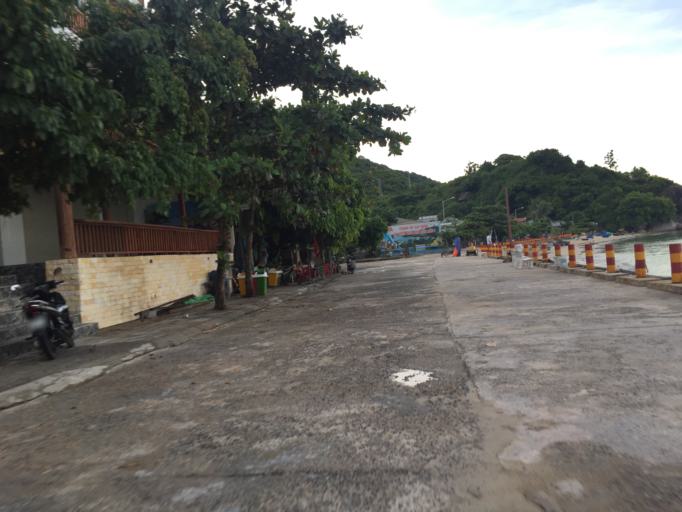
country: VN
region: Quang Nam
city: Hoi An
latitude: 15.9562
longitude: 108.5074
